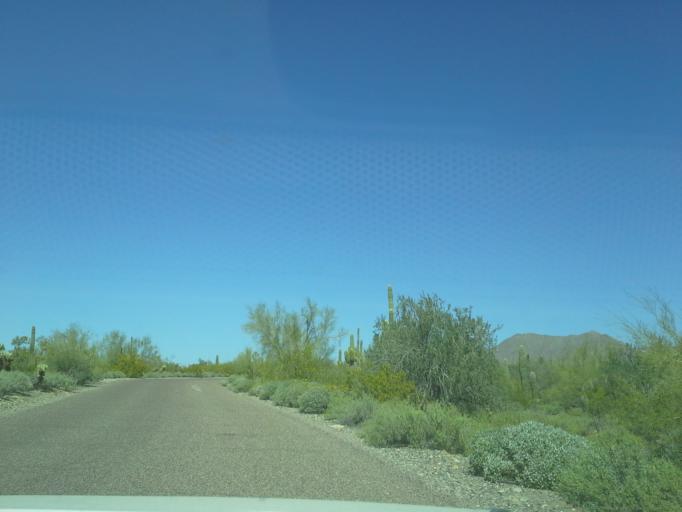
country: US
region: Arizona
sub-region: Maricopa County
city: Scottsdale
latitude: 33.6034
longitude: -111.8467
